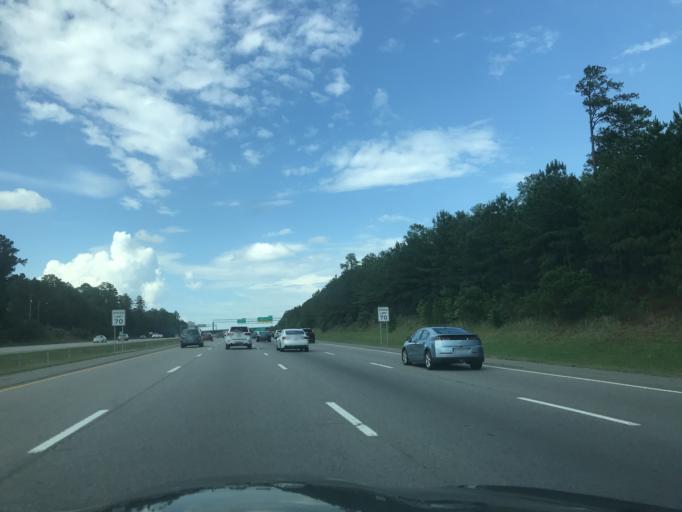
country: US
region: North Carolina
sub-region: Wake County
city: Morrisville
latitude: 35.8821
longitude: -78.8228
